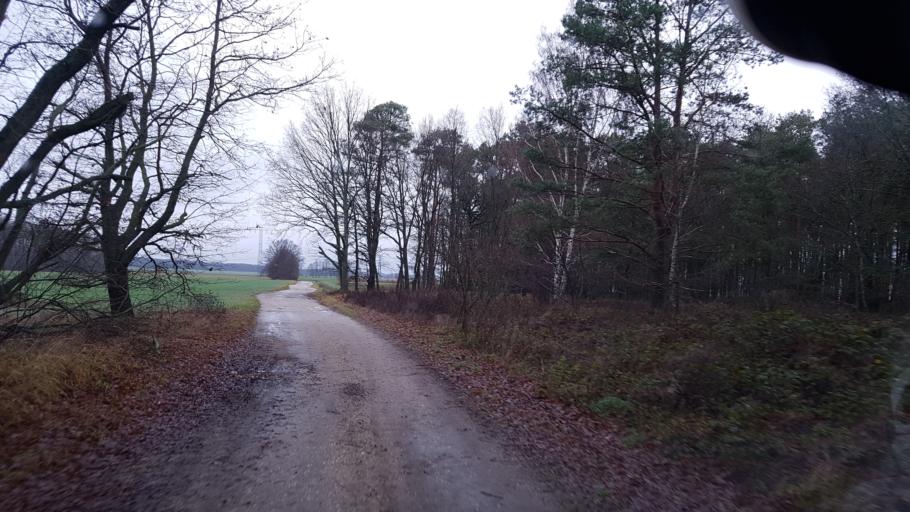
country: DE
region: Brandenburg
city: Sallgast
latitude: 51.6158
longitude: 13.8444
